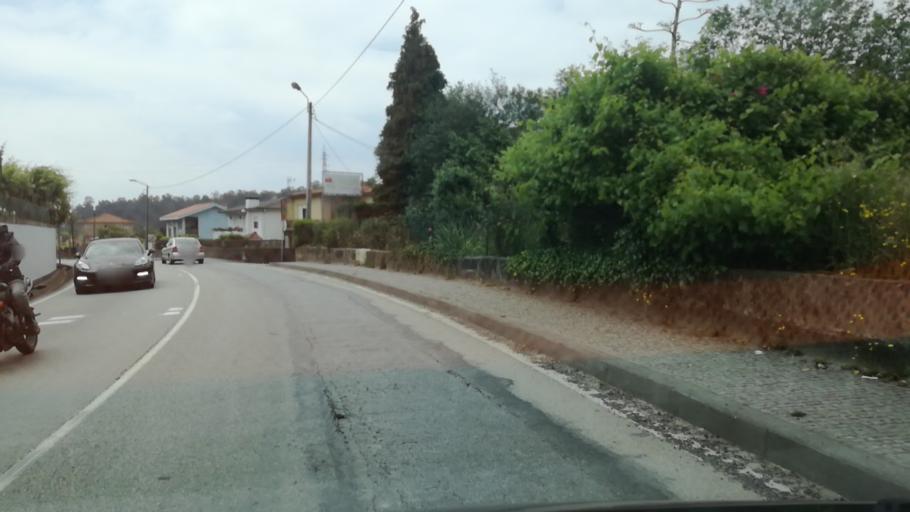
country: PT
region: Porto
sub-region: Trofa
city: Sao Romao do Coronado
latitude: 41.2968
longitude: -8.5997
